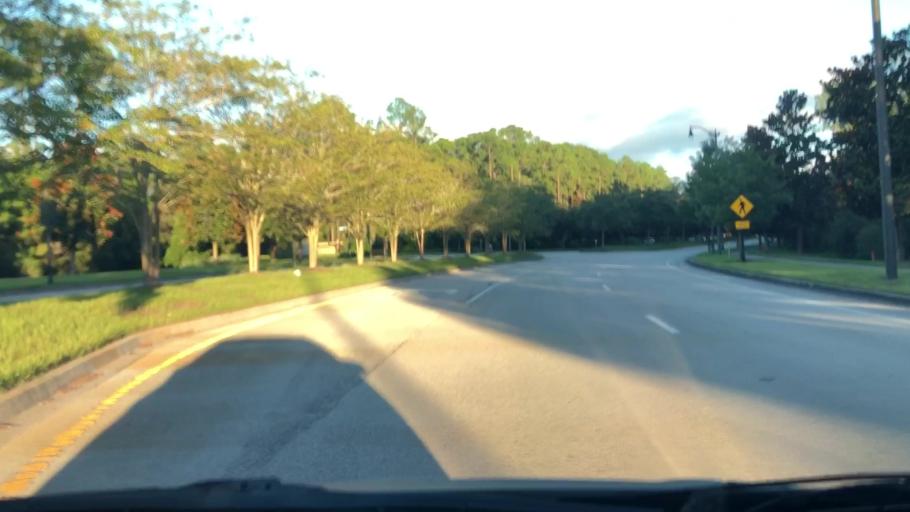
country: US
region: Florida
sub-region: Saint Johns County
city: Palm Valley
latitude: 30.1247
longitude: -81.4229
